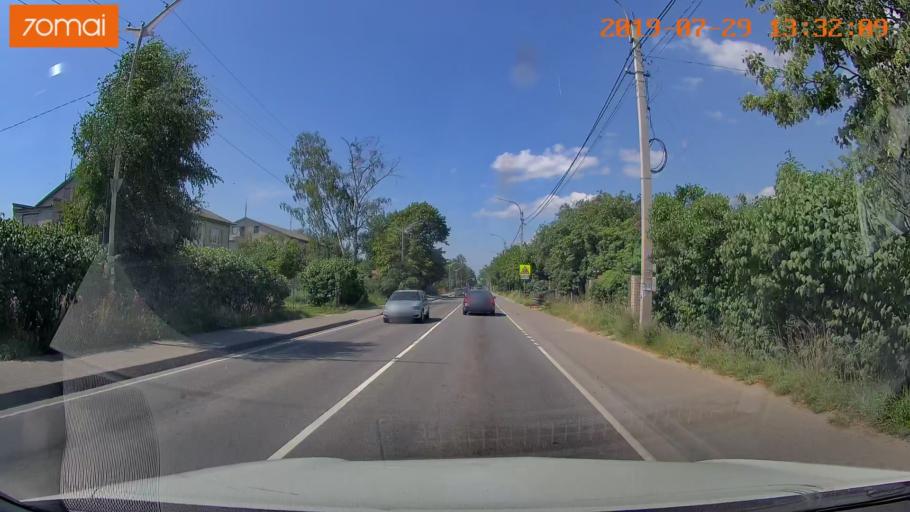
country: RU
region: Kaliningrad
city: Vzmorye
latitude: 54.6974
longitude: 20.2386
